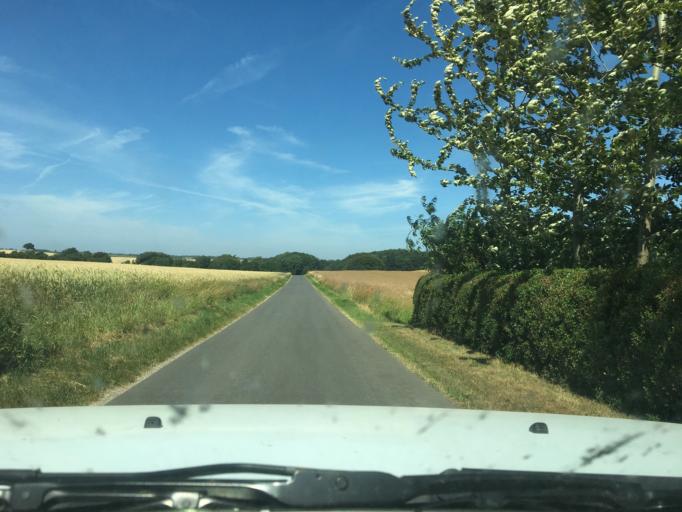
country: DK
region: Central Jutland
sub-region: Viborg Kommune
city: Bjerringbro
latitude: 56.5237
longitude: 9.6761
